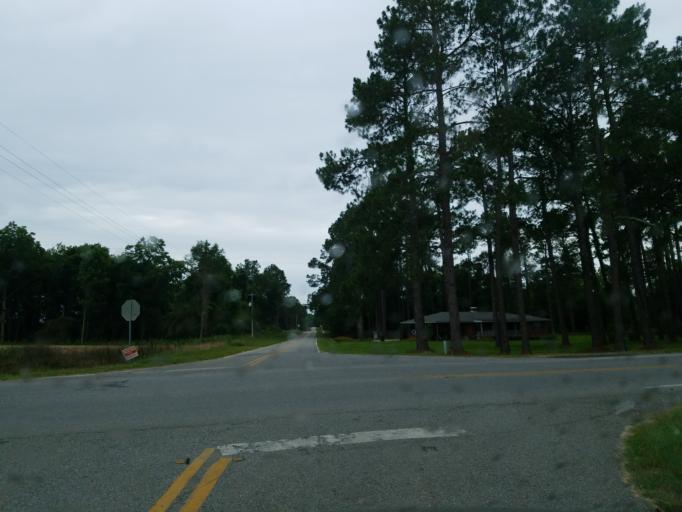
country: US
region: Georgia
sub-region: Crisp County
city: Cordele
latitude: 31.9505
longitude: -83.6987
